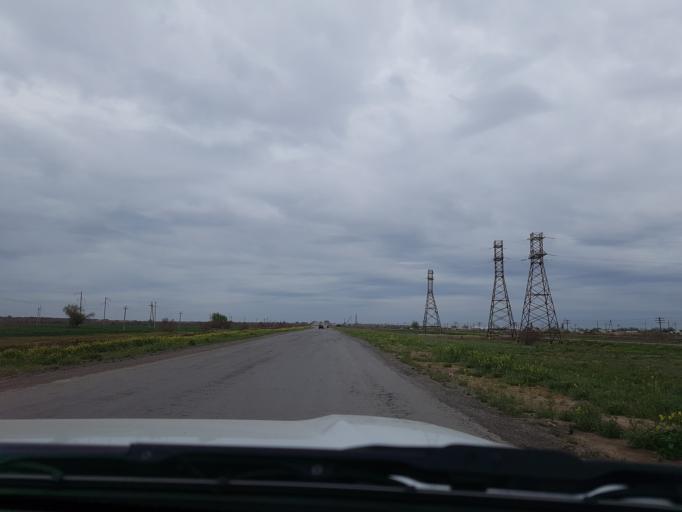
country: TM
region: Mary
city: Bayramaly
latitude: 37.7604
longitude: 62.5065
